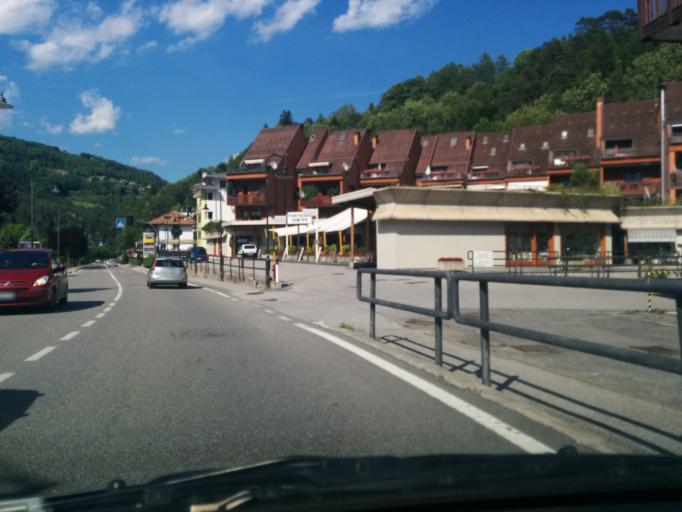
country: IT
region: Trentino-Alto Adige
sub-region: Provincia di Trento
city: Ponte Arche
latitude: 46.0364
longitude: 10.8750
